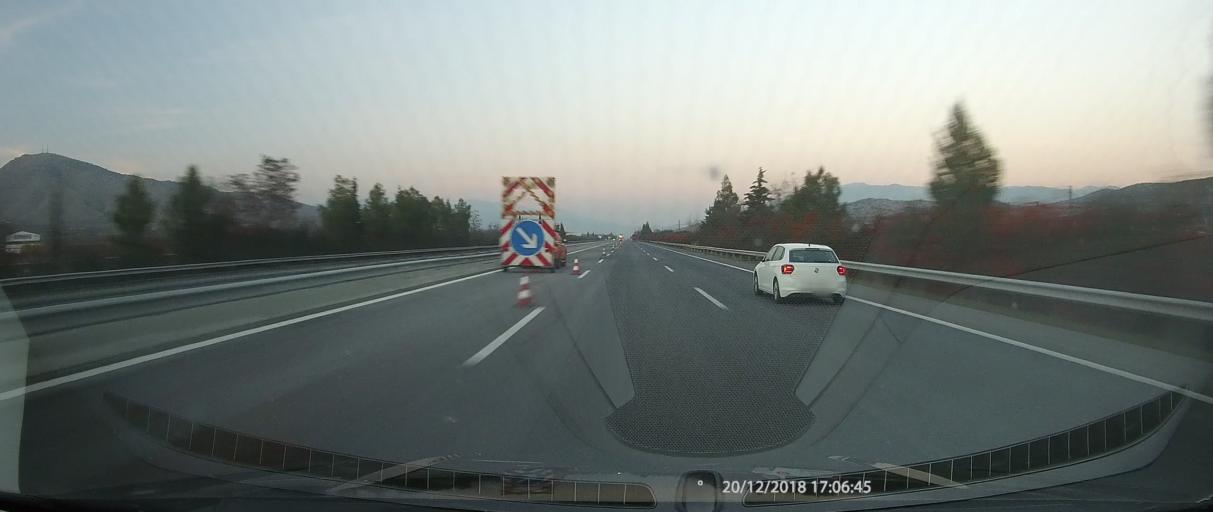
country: GR
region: Thessaly
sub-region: Nomos Larisis
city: Makrychori
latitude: 39.7649
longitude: 22.4812
